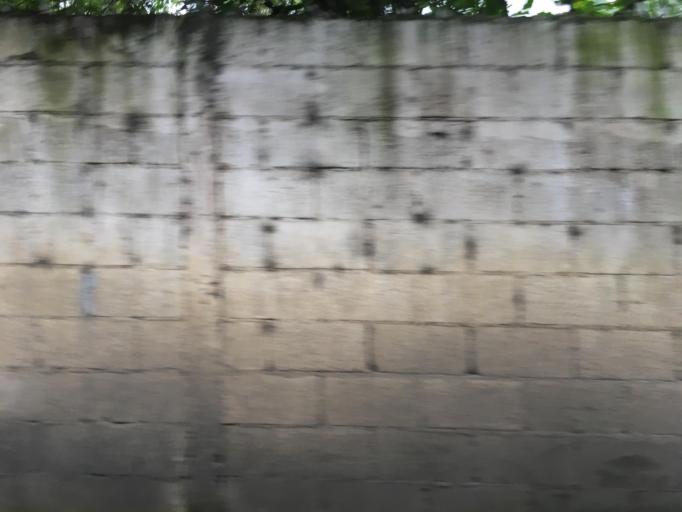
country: GT
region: Sacatepequez
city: Jocotenango
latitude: 14.5718
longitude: -90.7444
